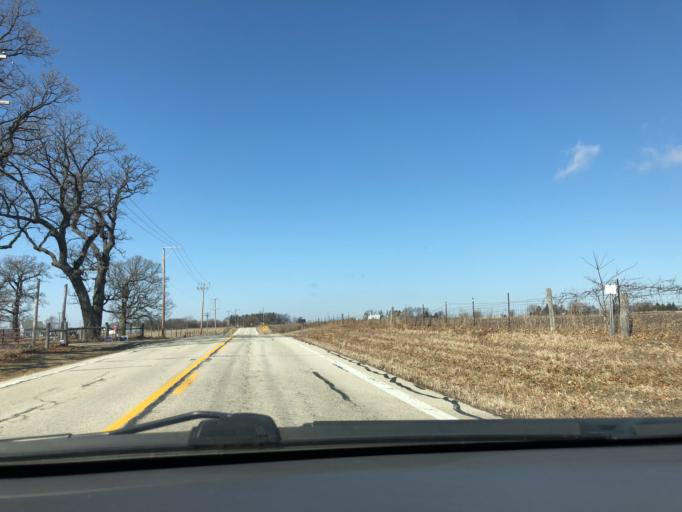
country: US
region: Illinois
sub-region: Kane County
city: Hampshire
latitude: 42.1335
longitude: -88.5306
